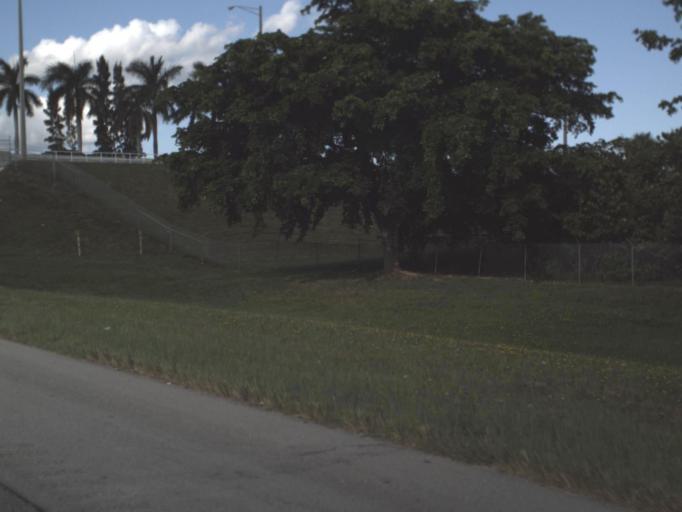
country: US
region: Florida
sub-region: Palm Beach County
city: Boca Pointe
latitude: 26.3169
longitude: -80.1699
